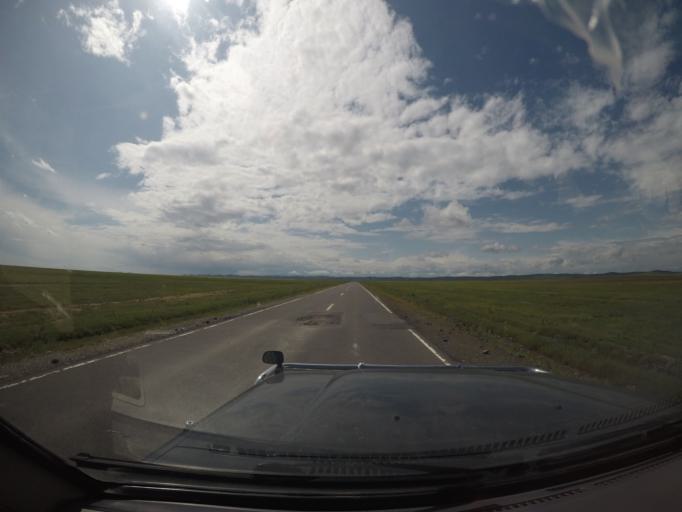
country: MN
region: Hentiy
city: Moron
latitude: 47.4193
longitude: 109.9797
